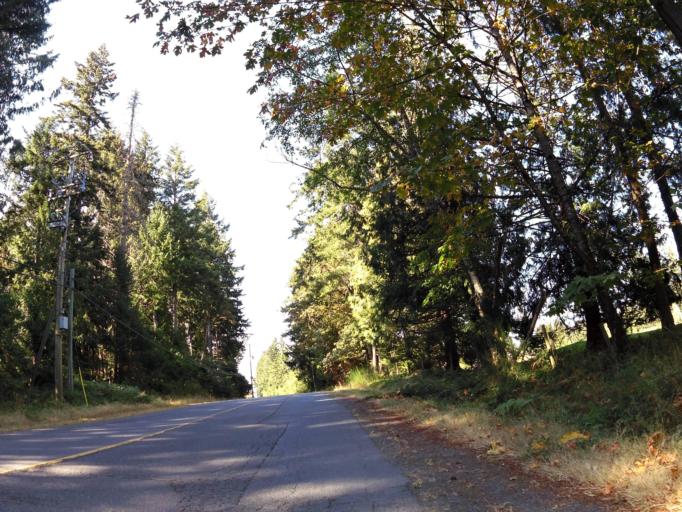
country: CA
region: British Columbia
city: North Saanich
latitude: 48.6832
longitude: -123.5510
